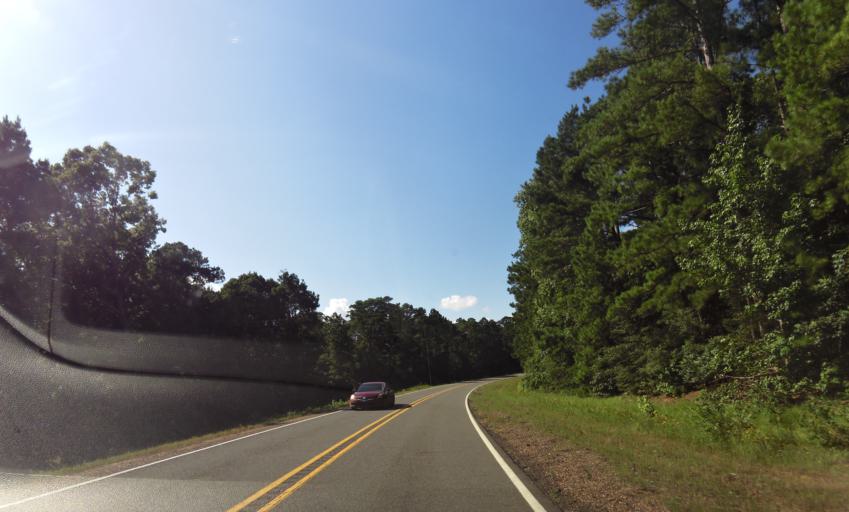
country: US
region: Louisiana
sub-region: Sabine Parish
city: Many
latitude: 31.4306
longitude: -93.5870
